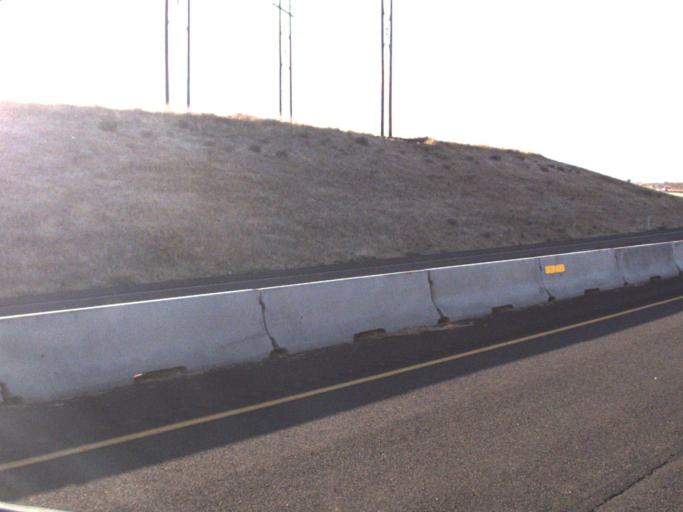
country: US
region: Washington
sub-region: Walla Walla County
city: College Place
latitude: 46.0725
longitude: -118.3785
